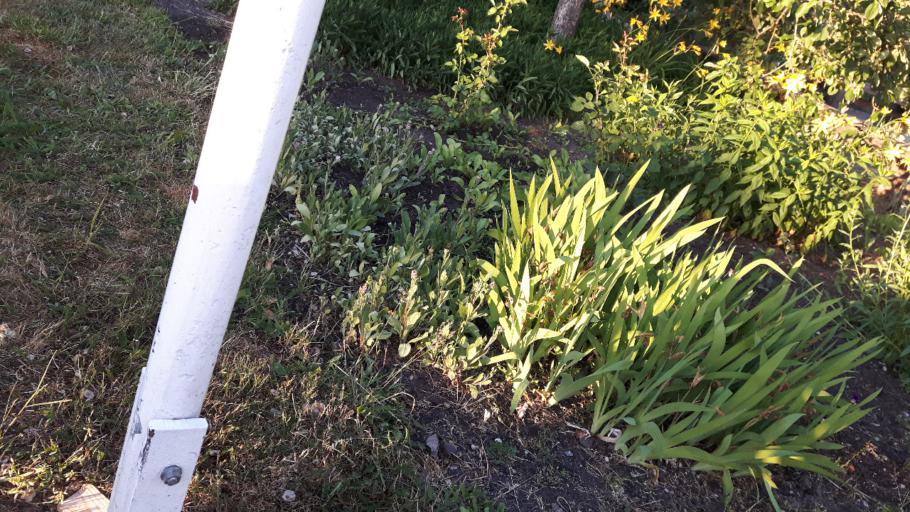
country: LV
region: Kuldigas Rajons
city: Kuldiga
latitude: 56.9695
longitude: 21.9798
